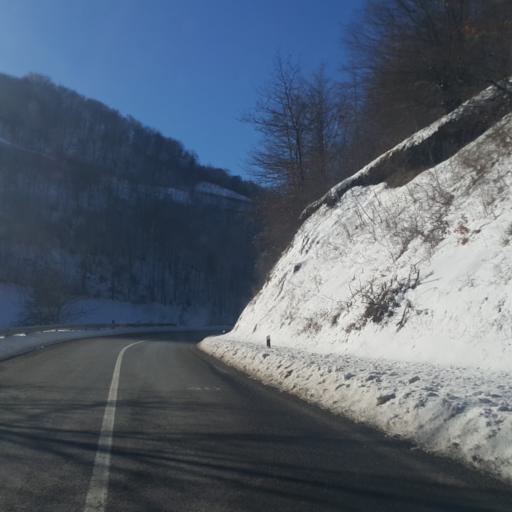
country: RS
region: Central Serbia
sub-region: Rasinski Okrug
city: Aleksandrovac
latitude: 43.3132
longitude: 20.9161
